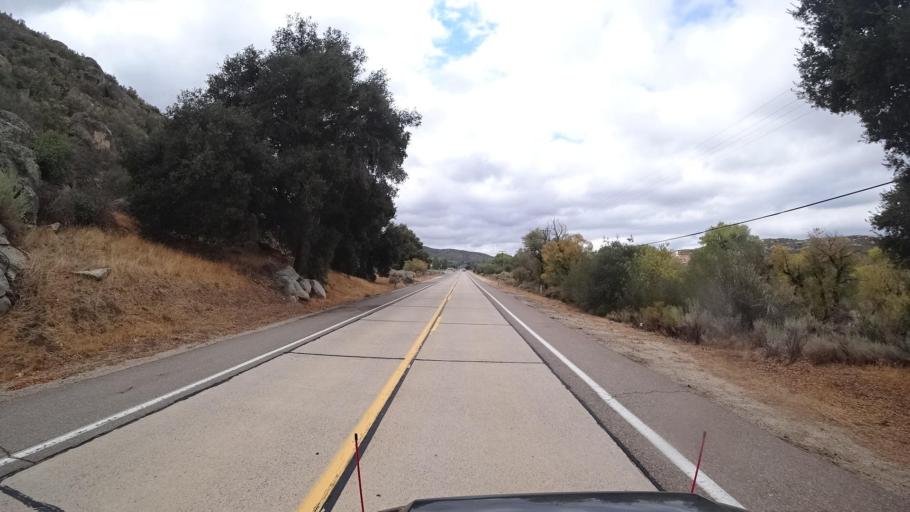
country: US
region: California
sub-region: San Diego County
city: Campo
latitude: 32.7225
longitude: -116.4459
